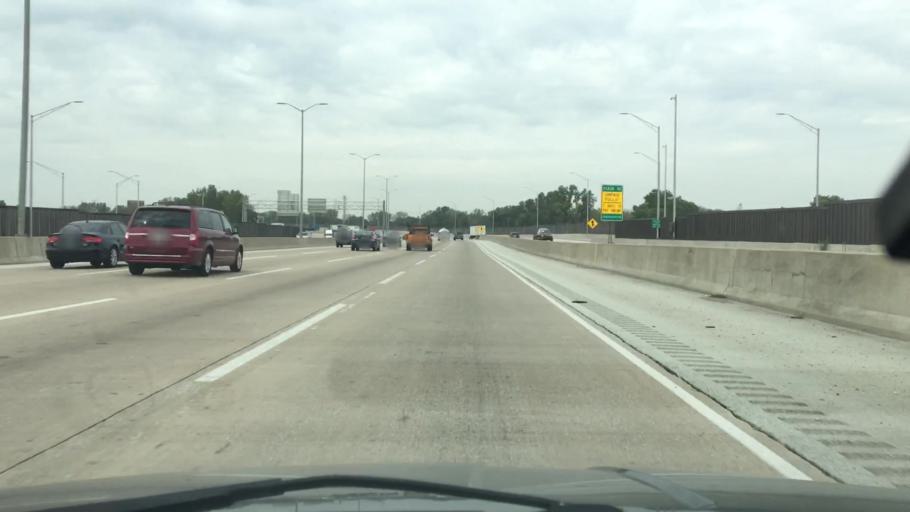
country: US
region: Illinois
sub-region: Cook County
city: Posen
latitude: 41.6268
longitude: -87.6915
